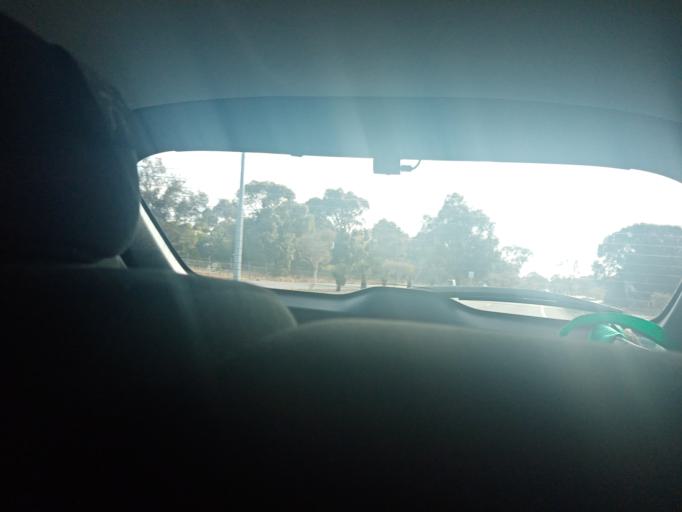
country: AU
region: Western Australia
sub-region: City of Cockburn
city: South Lake
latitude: -32.1251
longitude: 115.8343
